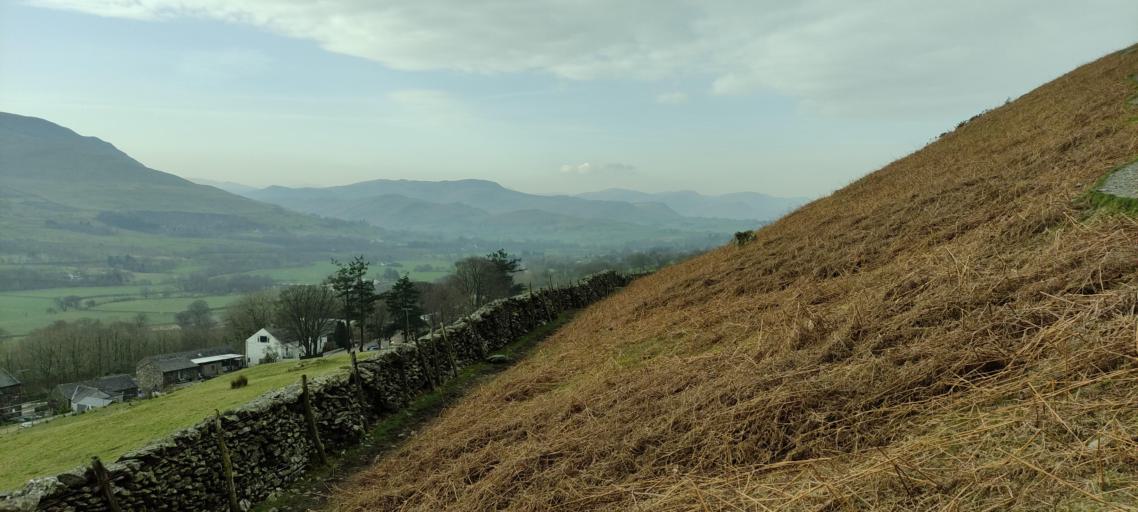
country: GB
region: England
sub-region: Cumbria
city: Keswick
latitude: 54.6312
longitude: -3.0308
